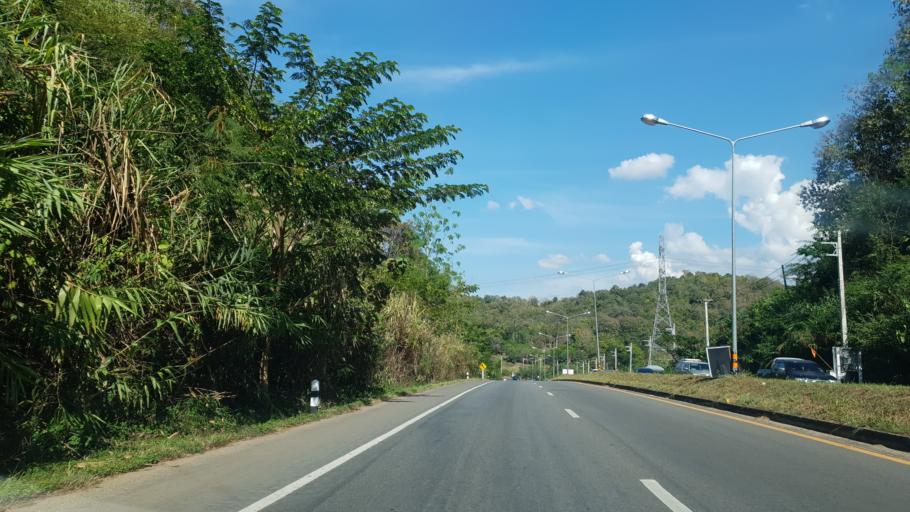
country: TH
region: Phrae
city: Den Chai
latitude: 17.8847
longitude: 100.0470
